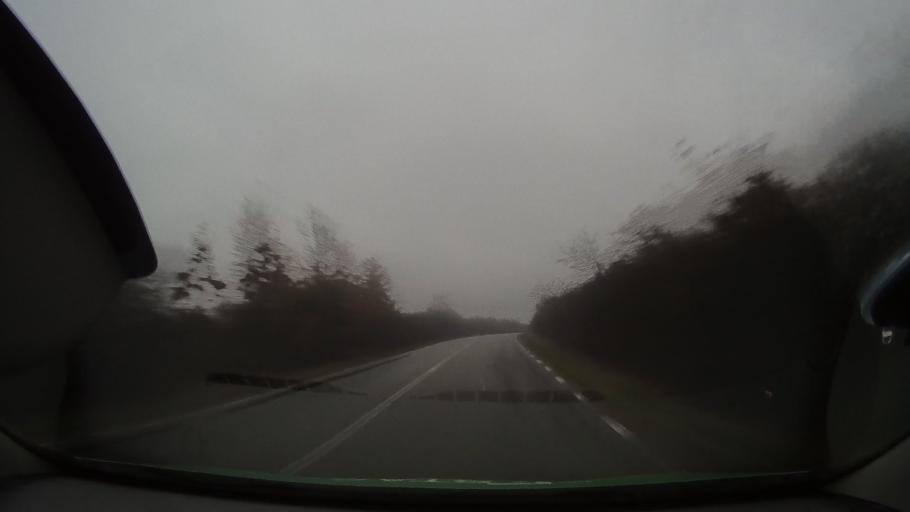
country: RO
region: Arad
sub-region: Comuna Craiova
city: Craiova
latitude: 46.6005
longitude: 21.9688
